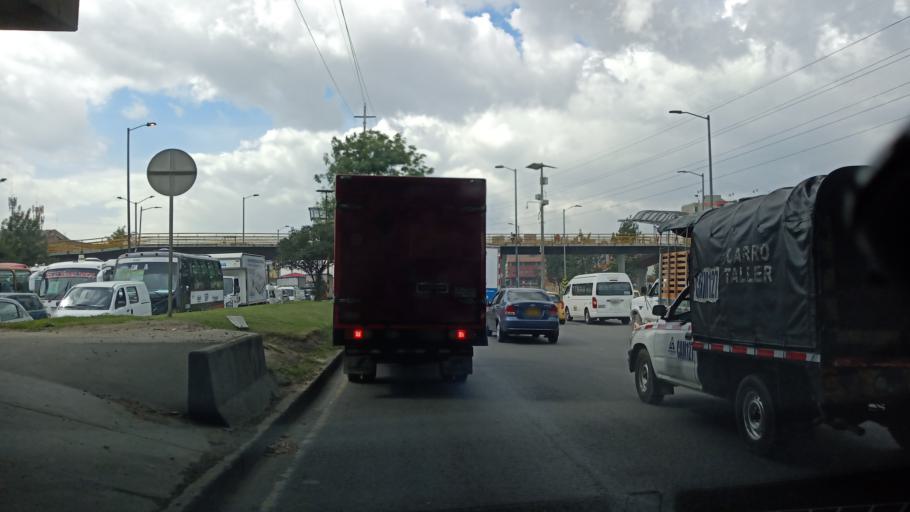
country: CO
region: Bogota D.C.
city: Bogota
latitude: 4.6594
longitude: -74.1359
